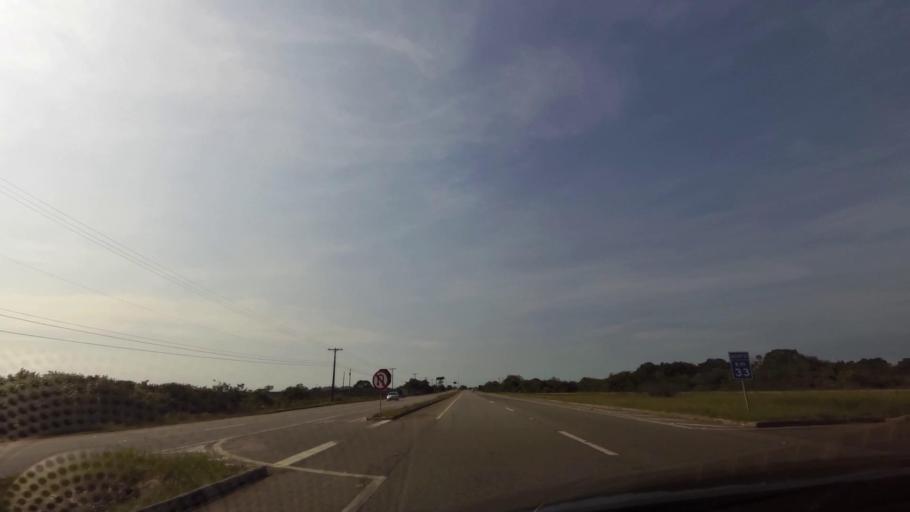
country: BR
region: Espirito Santo
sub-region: Guarapari
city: Guarapari
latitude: -20.5650
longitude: -40.4091
